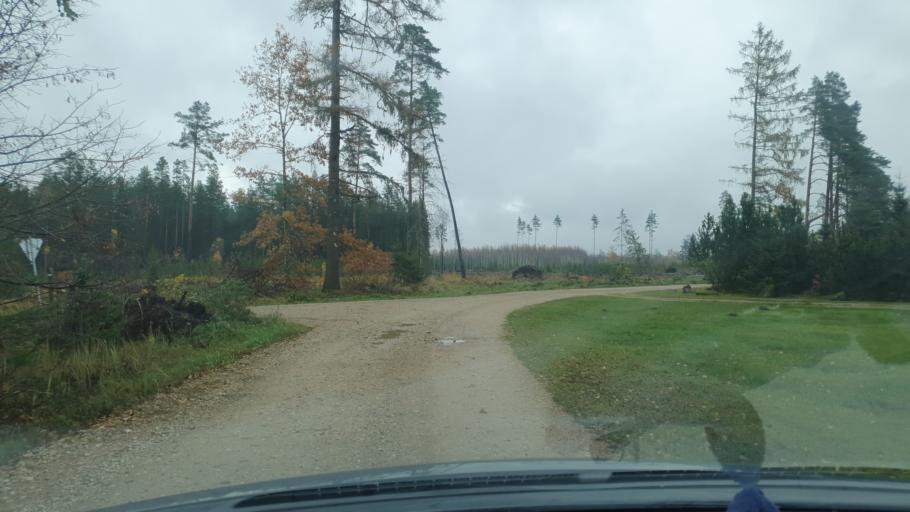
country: EE
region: Viljandimaa
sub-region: Karksi vald
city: Karksi-Nuia
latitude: 57.9922
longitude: 25.6398
